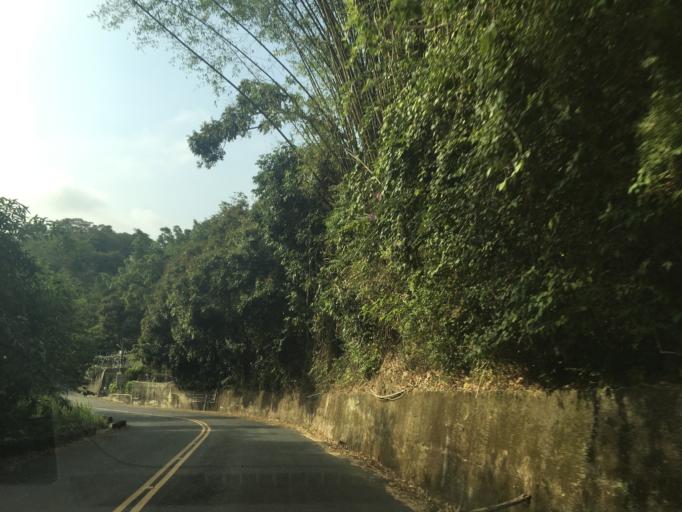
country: TW
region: Taiwan
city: Fengyuan
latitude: 24.2306
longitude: 120.7507
